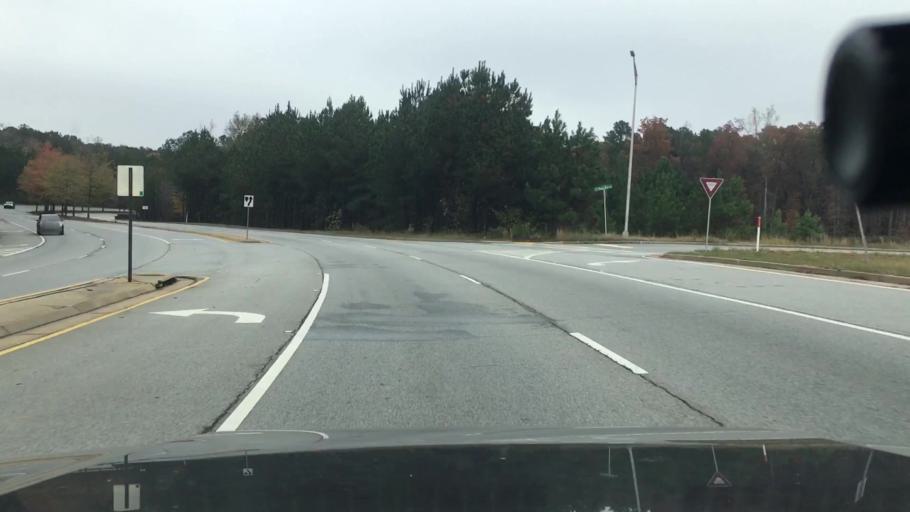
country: US
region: Georgia
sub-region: Coweta County
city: East Newnan
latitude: 33.3822
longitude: -84.7626
